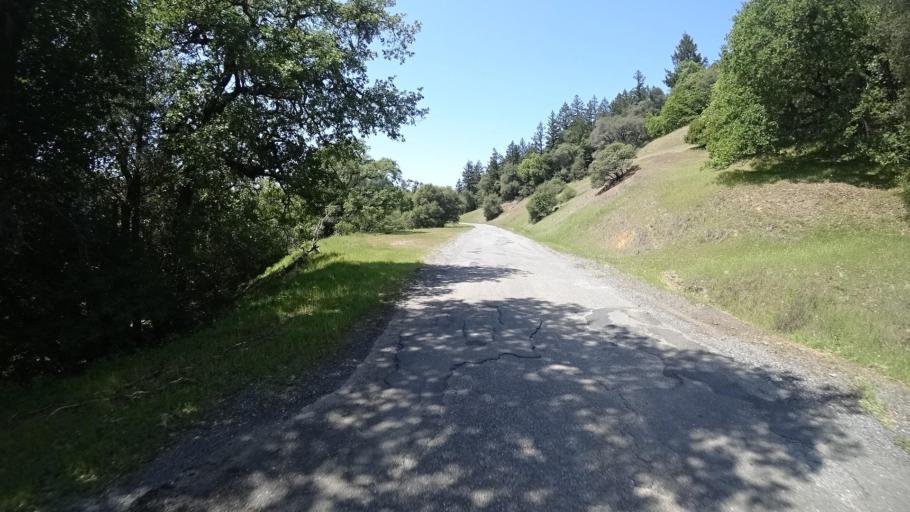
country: US
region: California
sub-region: Humboldt County
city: Redway
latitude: 40.2272
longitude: -123.6427
